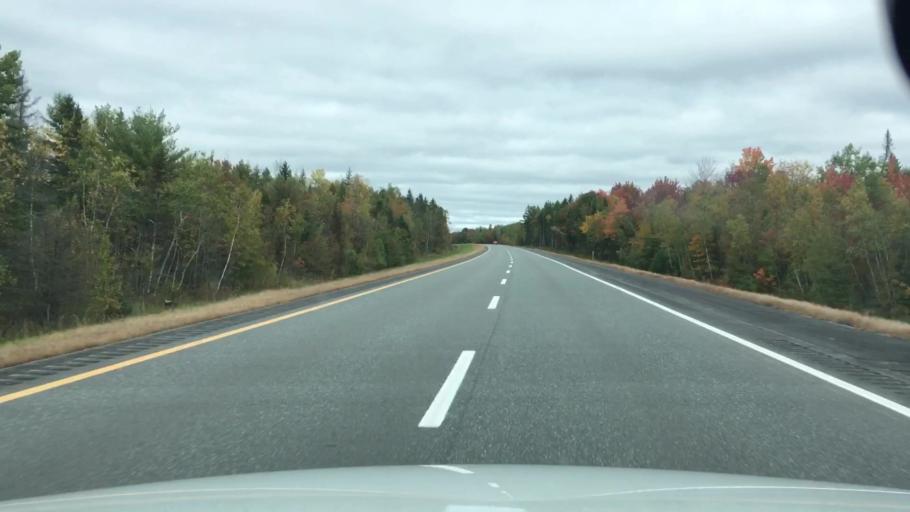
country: US
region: Maine
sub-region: Waldo County
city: Burnham
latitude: 44.7084
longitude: -69.4518
